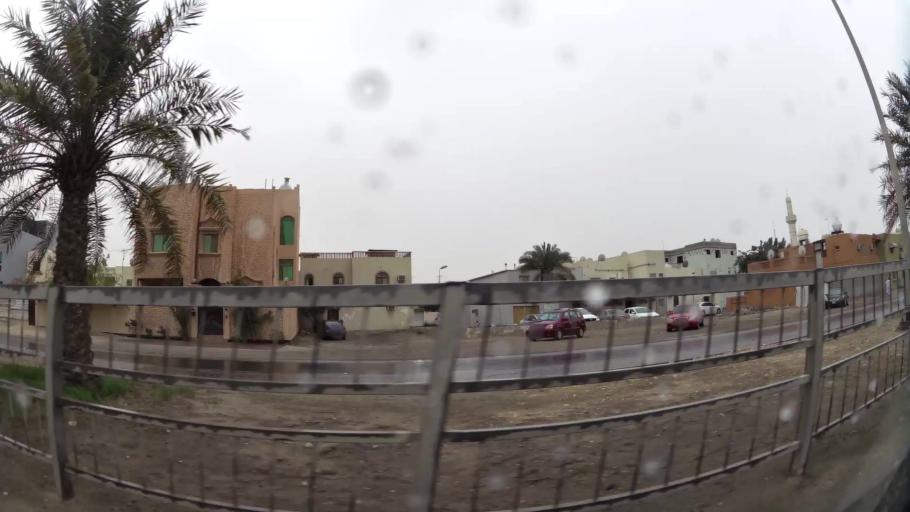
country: BH
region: Northern
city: Madinat `Isa
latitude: 26.1621
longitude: 50.5683
